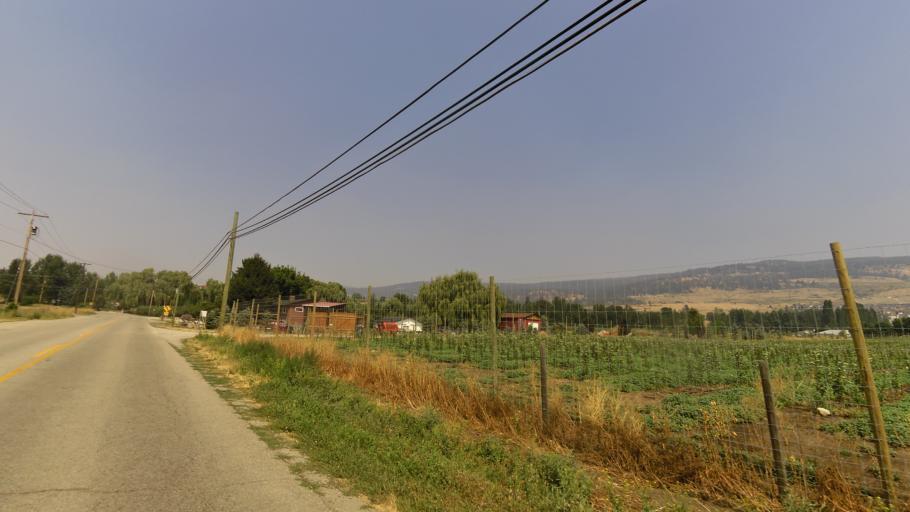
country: CA
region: British Columbia
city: Kelowna
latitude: 49.9387
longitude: -119.3641
